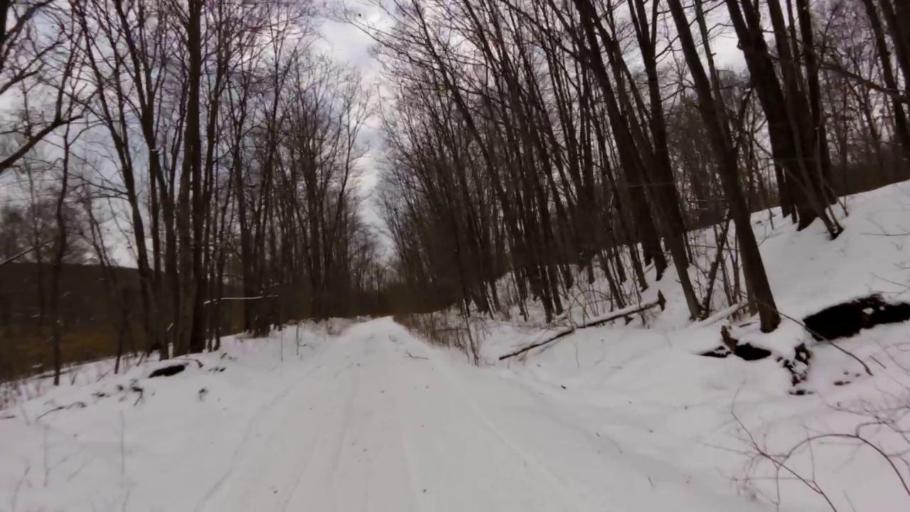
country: US
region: Pennsylvania
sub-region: McKean County
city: Foster Brook
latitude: 42.0617
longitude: -78.6381
